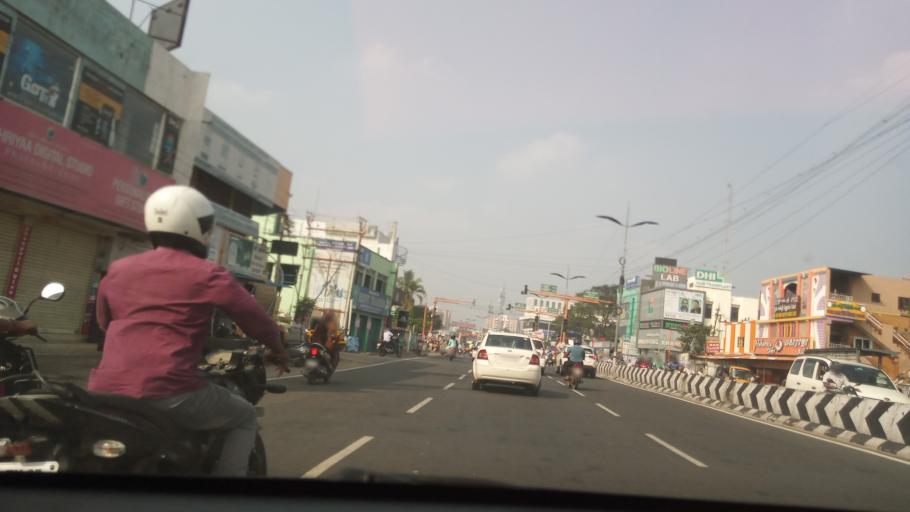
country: IN
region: Tamil Nadu
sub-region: Coimbatore
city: Coimbatore
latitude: 11.0220
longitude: 76.9969
